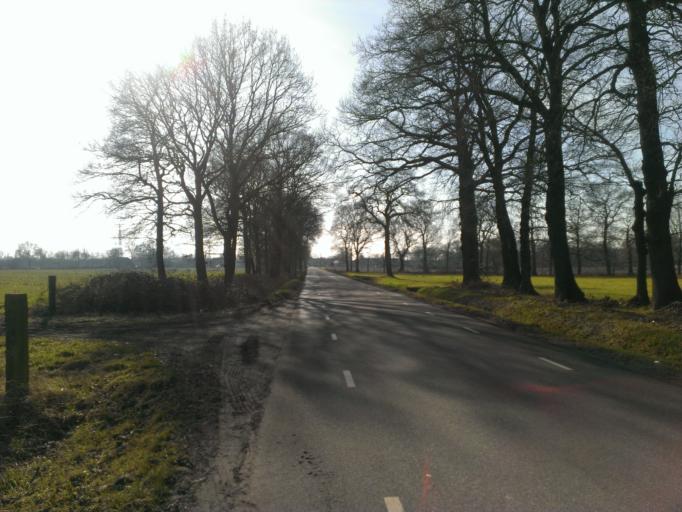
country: NL
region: Drenthe
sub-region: Gemeente Hoogeveen
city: Hoogeveen
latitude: 52.7456
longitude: 6.4776
